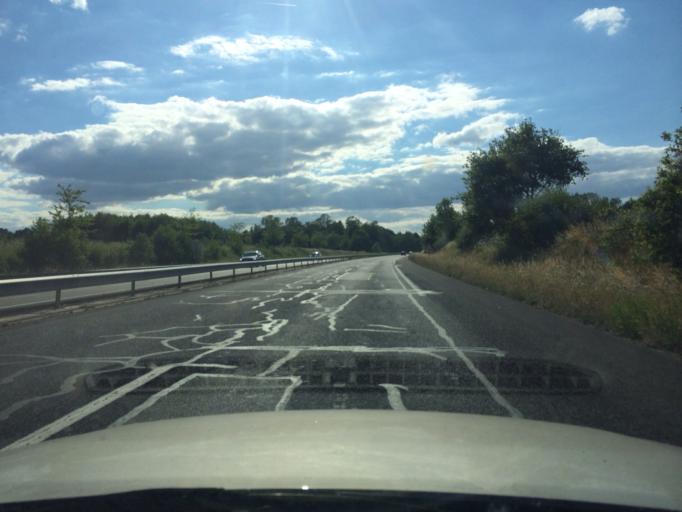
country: FR
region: Lorraine
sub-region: Departement de Meurthe-et-Moselle
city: Chanteheux
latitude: 48.5743
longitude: 6.6210
